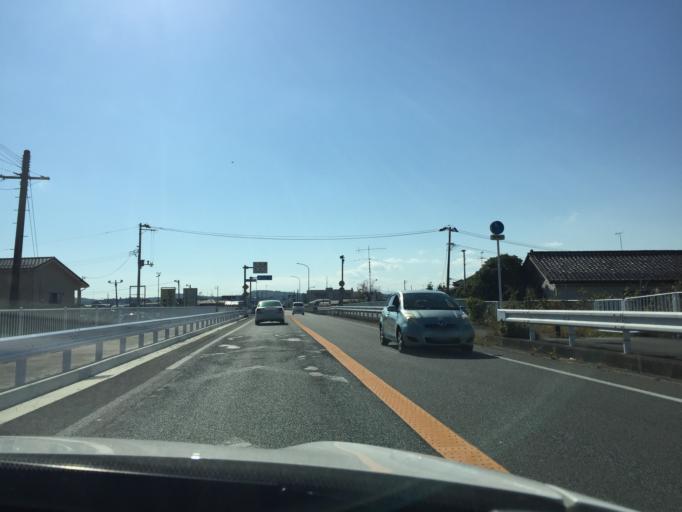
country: JP
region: Miyagi
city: Marumori
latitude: 37.7975
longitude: 140.9287
